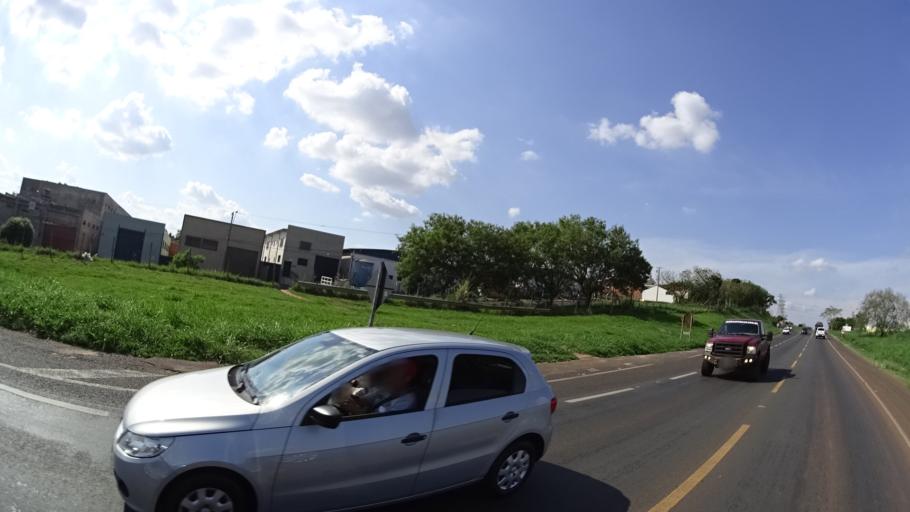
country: BR
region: Sao Paulo
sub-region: Sao Jose Do Rio Preto
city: Sao Jose do Rio Preto
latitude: -20.8468
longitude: -49.3745
